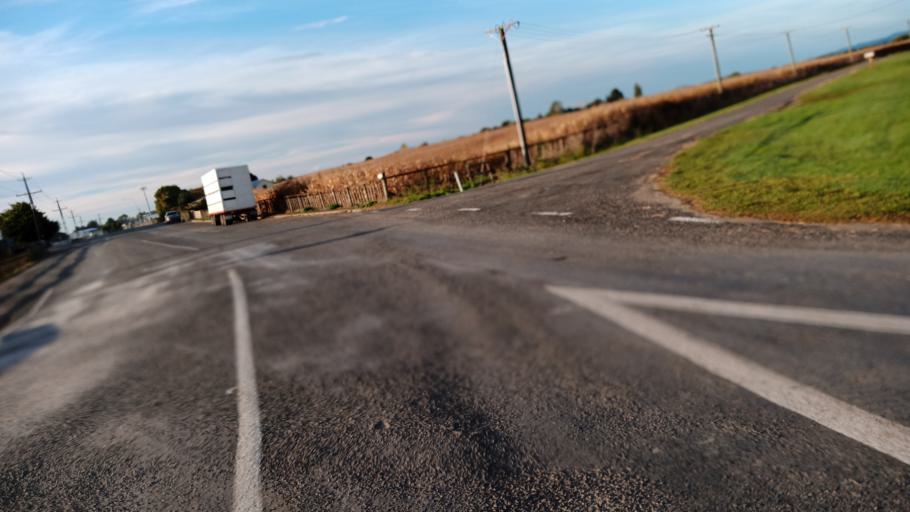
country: NZ
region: Gisborne
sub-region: Gisborne District
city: Gisborne
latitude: -38.6517
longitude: 177.9423
